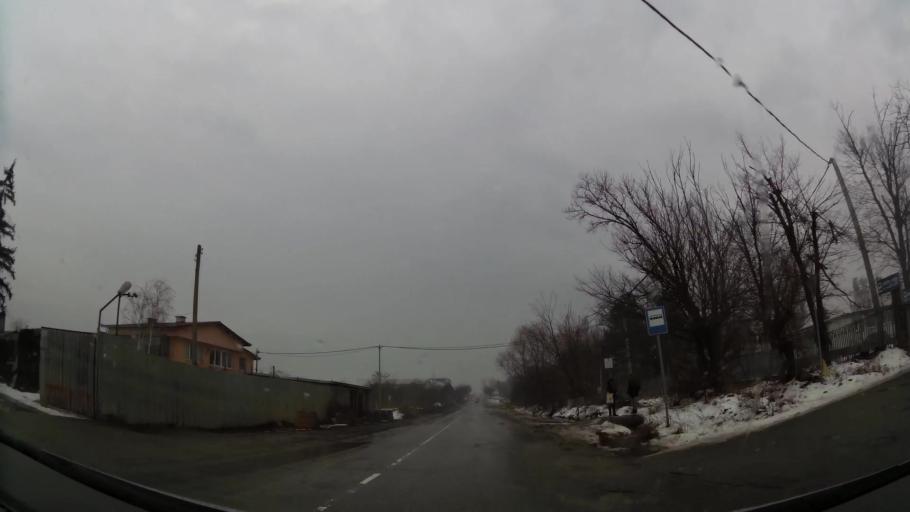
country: BG
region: Sofiya
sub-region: Obshtina Bozhurishte
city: Bozhurishte
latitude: 42.6955
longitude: 23.2444
